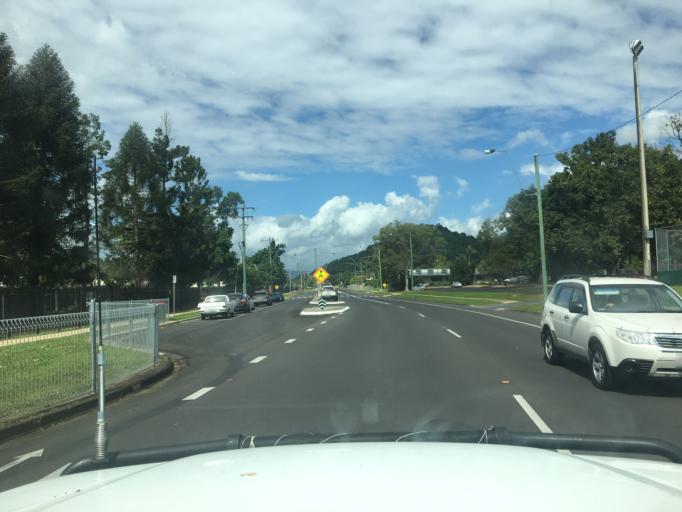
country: AU
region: Queensland
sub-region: Cairns
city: Woree
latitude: -16.9599
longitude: 145.7404
